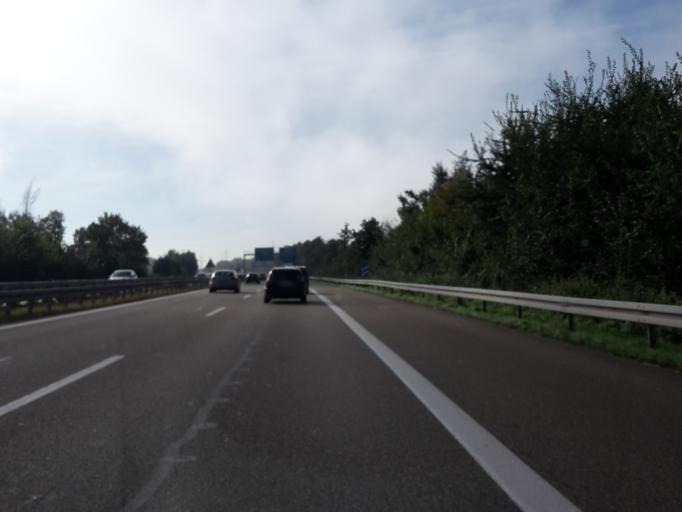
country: DE
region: Baden-Wuerttemberg
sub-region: Karlsruhe Region
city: Hemsbach
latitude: 49.5581
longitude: 8.6287
